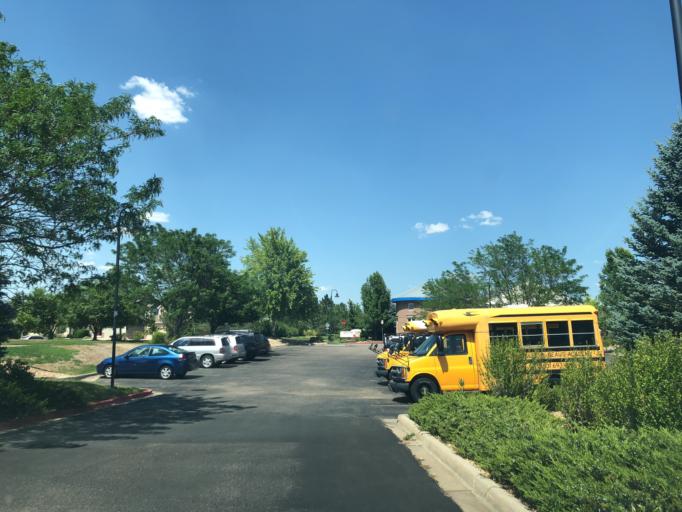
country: US
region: Colorado
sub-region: Arapahoe County
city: Dove Valley
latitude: 39.6046
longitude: -104.7747
